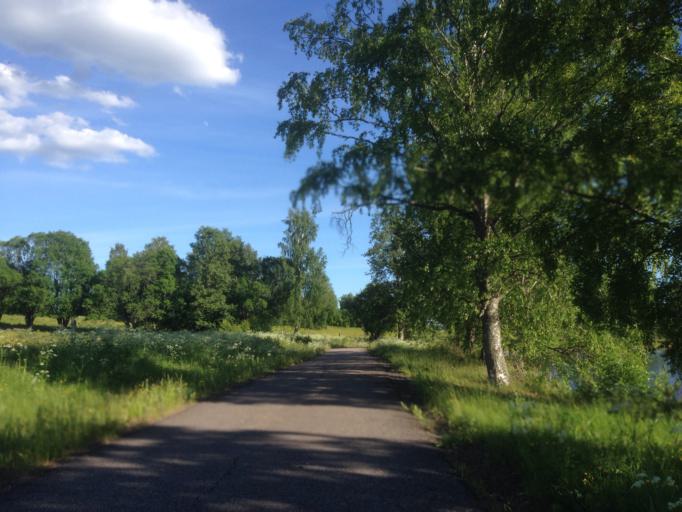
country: SE
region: Dalarna
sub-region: Ludvika Kommun
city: Ludvika
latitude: 60.1073
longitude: 15.2111
